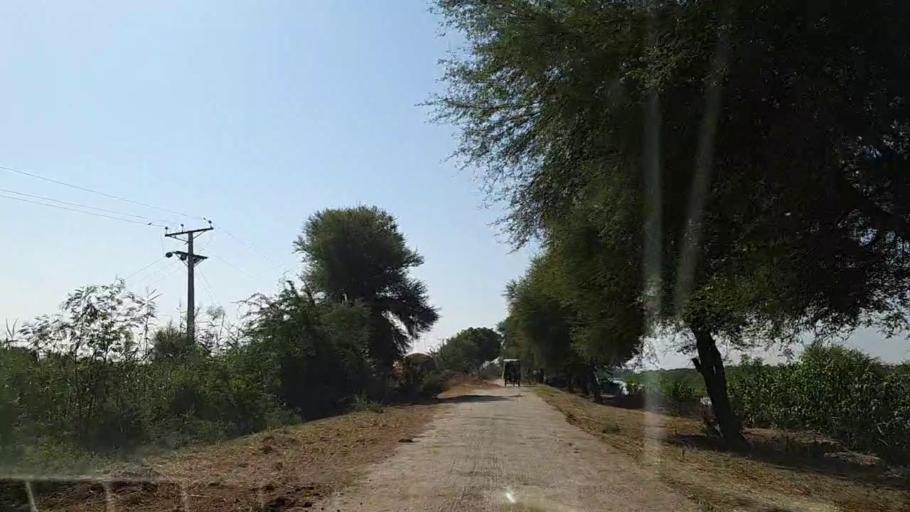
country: PK
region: Sindh
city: Chuhar Jamali
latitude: 24.5833
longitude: 68.0475
